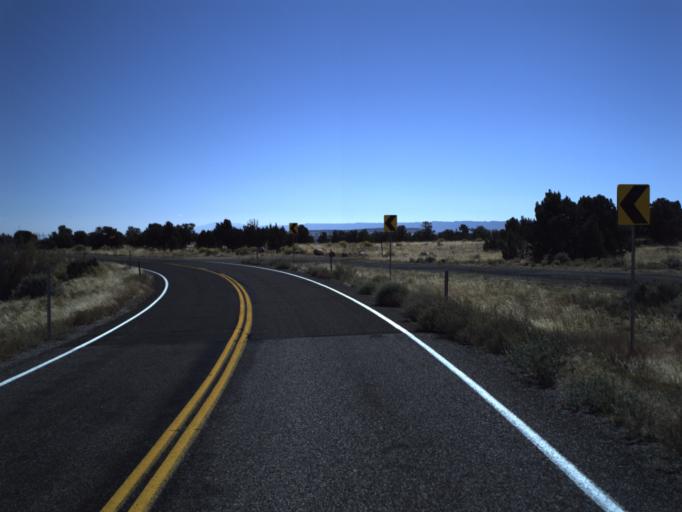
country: US
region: Utah
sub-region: Wayne County
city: Loa
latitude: 37.8459
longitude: -111.4273
